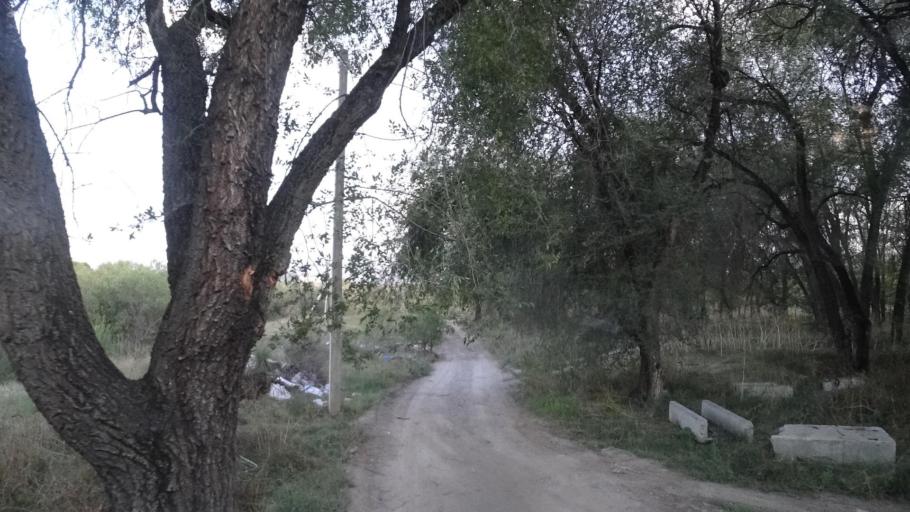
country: KZ
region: Almaty Oblysy
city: Pervomayskiy
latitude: 43.3362
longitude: 76.9985
